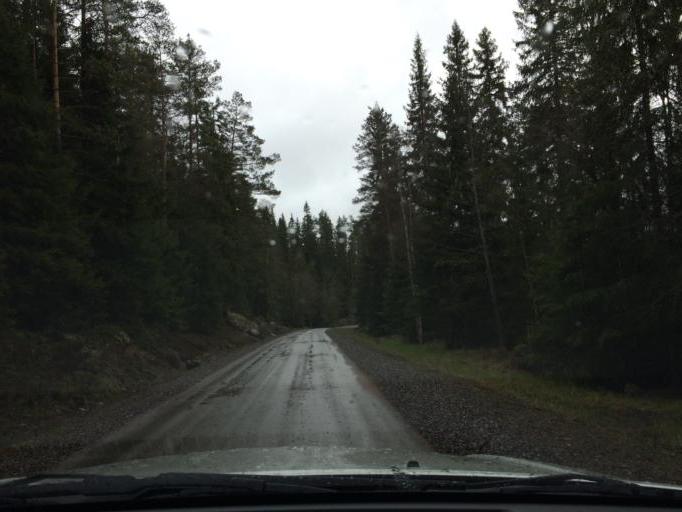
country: SE
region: Dalarna
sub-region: Ludvika Kommun
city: Abborrberget
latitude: 60.0234
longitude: 14.6080
